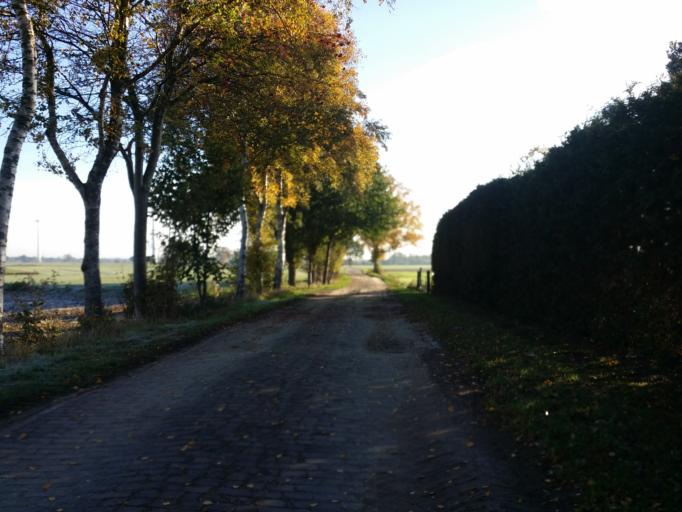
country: DE
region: Lower Saxony
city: Grasberg
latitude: 53.1915
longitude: 9.0305
